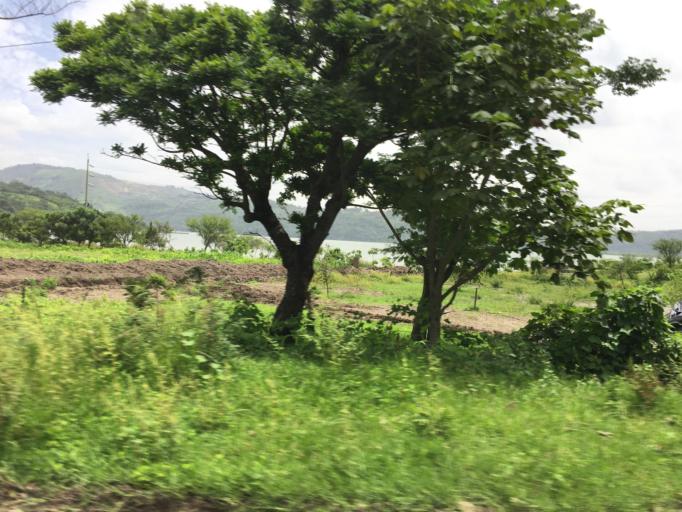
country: GT
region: Guatemala
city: Amatitlan
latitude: 14.4606
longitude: -90.5848
